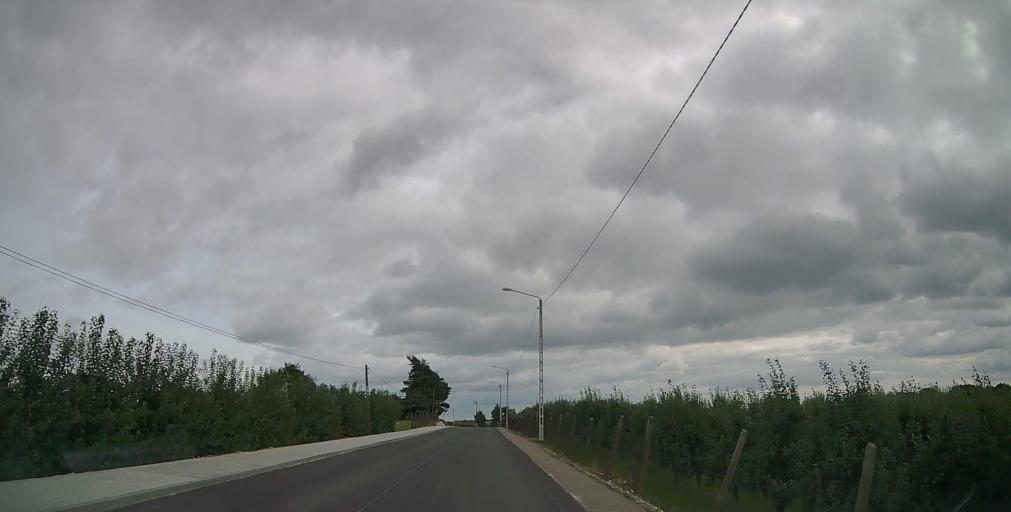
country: PL
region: Masovian Voivodeship
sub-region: Powiat grojecki
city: Belsk Duzy
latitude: 51.8139
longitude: 20.8314
